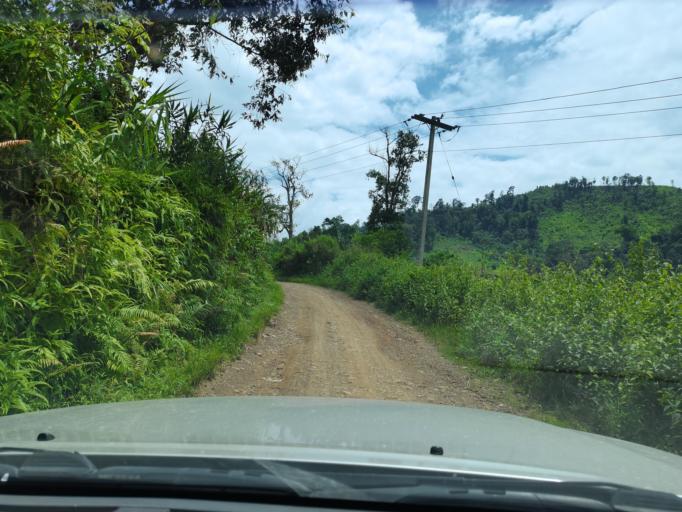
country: LA
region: Loungnamtha
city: Muang Long
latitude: 20.7291
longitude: 101.0142
